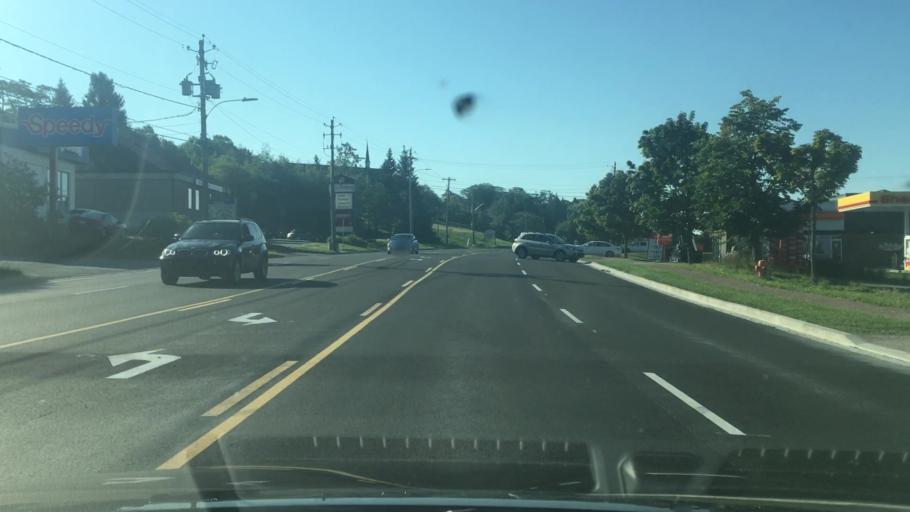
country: CA
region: Nova Scotia
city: Dartmouth
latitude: 44.7401
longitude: -63.6548
